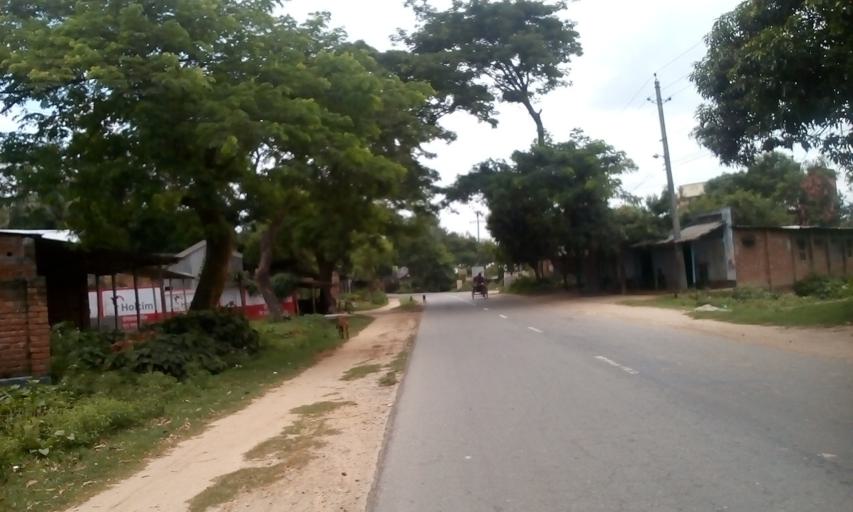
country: BD
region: Rangpur Division
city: Parbatipur
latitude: 25.3987
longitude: 88.9857
